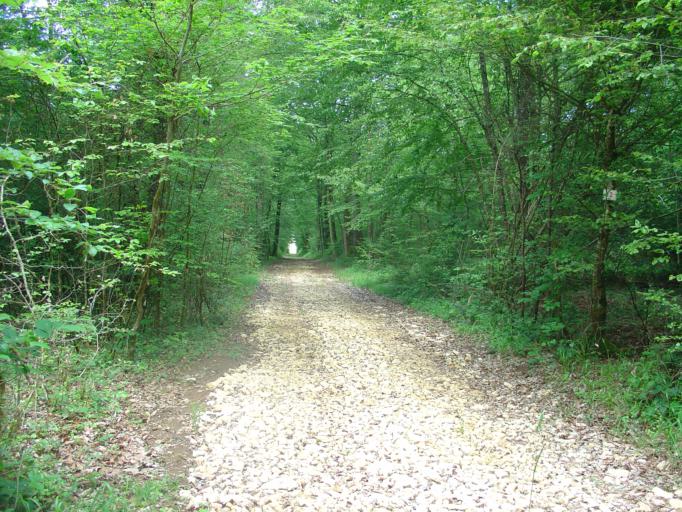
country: FR
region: Lorraine
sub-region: Departement de Meurthe-et-Moselle
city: Montauville
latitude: 48.8455
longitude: 5.9050
